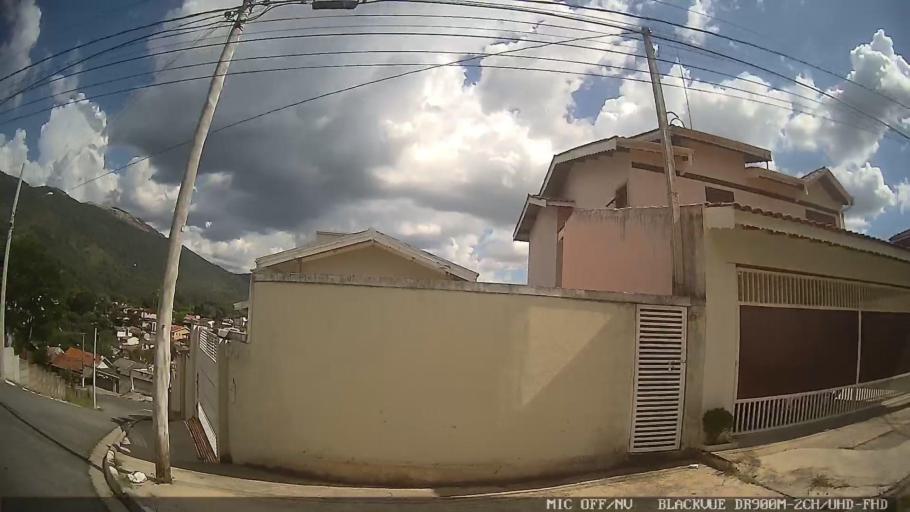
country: BR
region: Sao Paulo
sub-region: Atibaia
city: Atibaia
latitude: -23.1488
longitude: -46.5511
